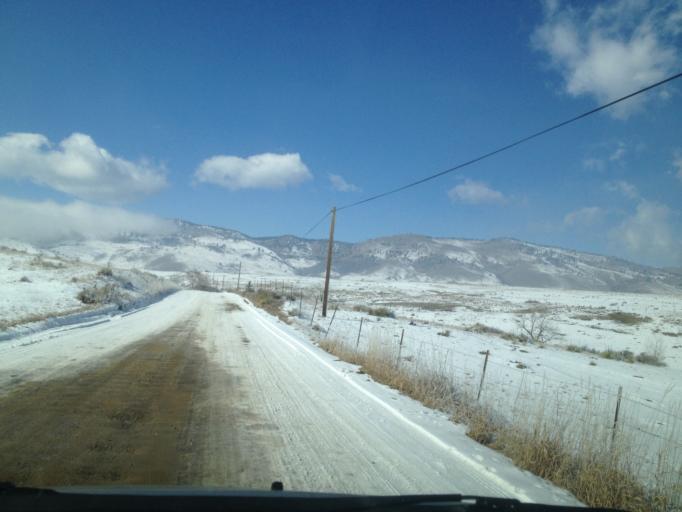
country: US
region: Colorado
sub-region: Boulder County
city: Boulder
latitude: 40.0799
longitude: -105.2652
